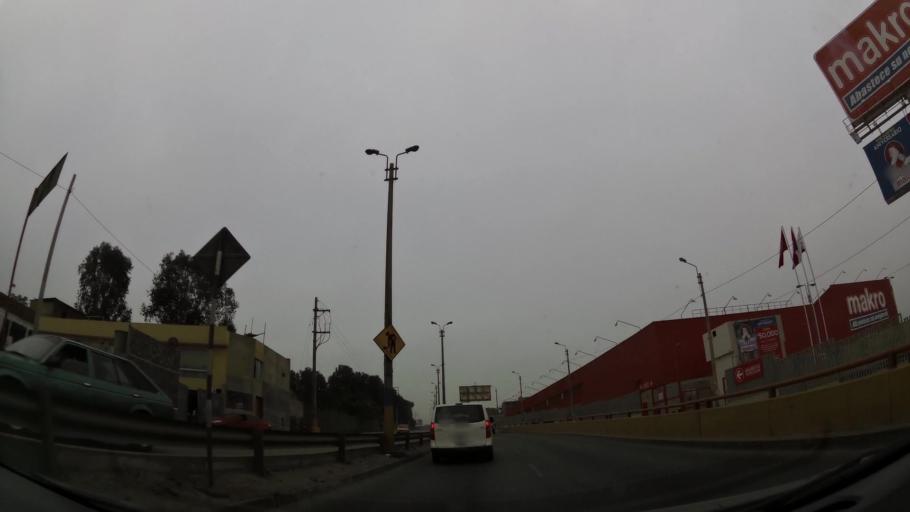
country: PE
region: Lima
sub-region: Lima
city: Surco
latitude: -12.1925
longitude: -76.9714
